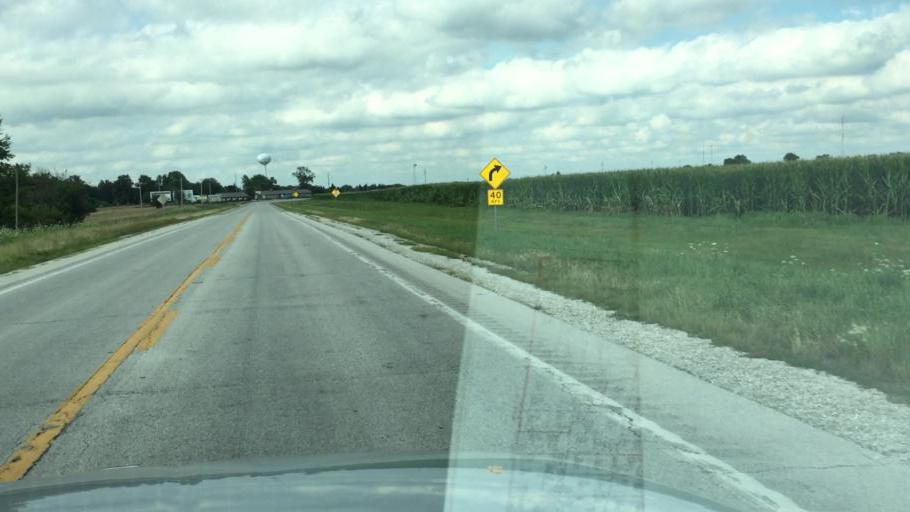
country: US
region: Illinois
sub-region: Hancock County
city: Carthage
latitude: 40.4116
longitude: -91.1574
